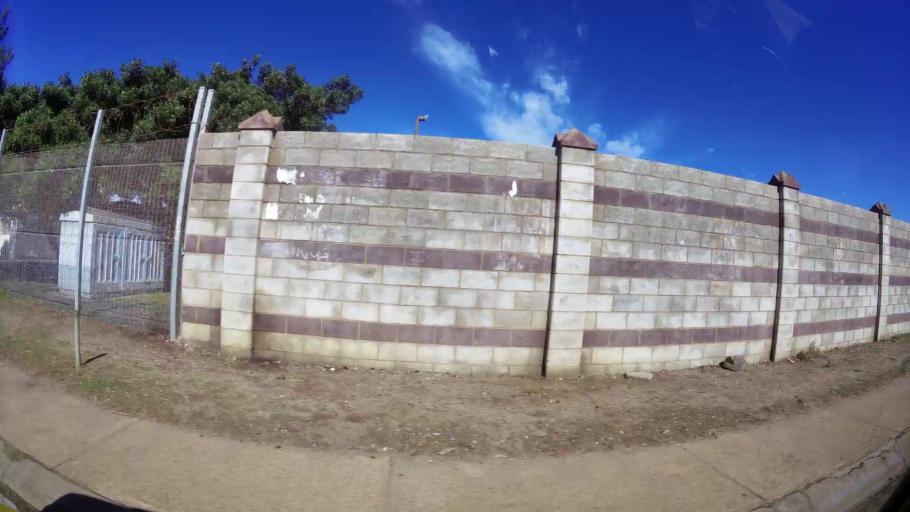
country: ZA
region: Eastern Cape
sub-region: Cacadu District Municipality
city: Jeffrey's Bay
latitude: -34.0585
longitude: 24.9215
